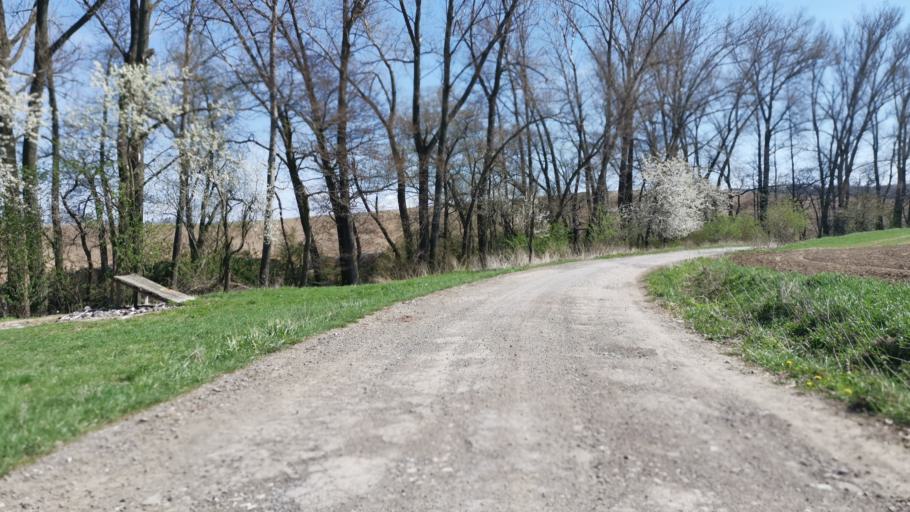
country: SK
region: Trnavsky
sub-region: Okres Skalica
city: Skalica
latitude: 48.7523
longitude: 17.2851
